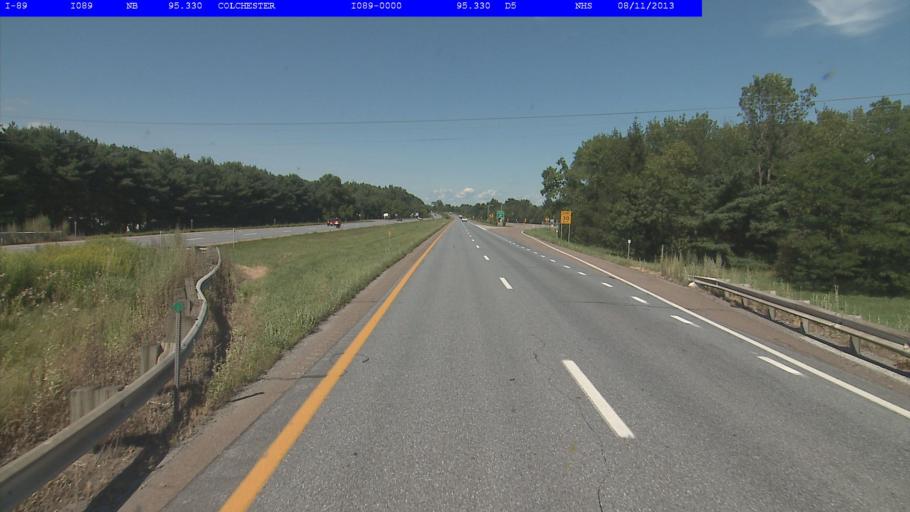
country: US
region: Vermont
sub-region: Chittenden County
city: Colchester
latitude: 44.5547
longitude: -73.1844
